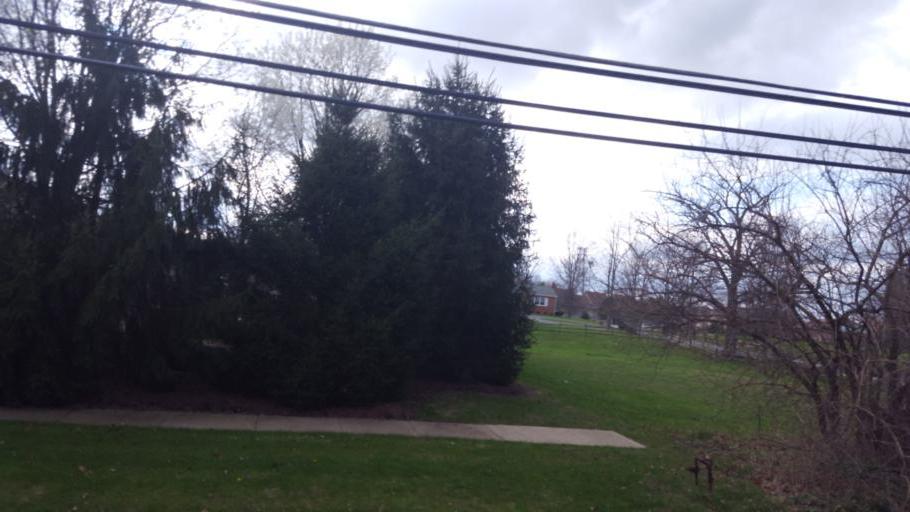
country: US
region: Ohio
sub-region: Delaware County
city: Powell
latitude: 40.1645
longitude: -83.0762
